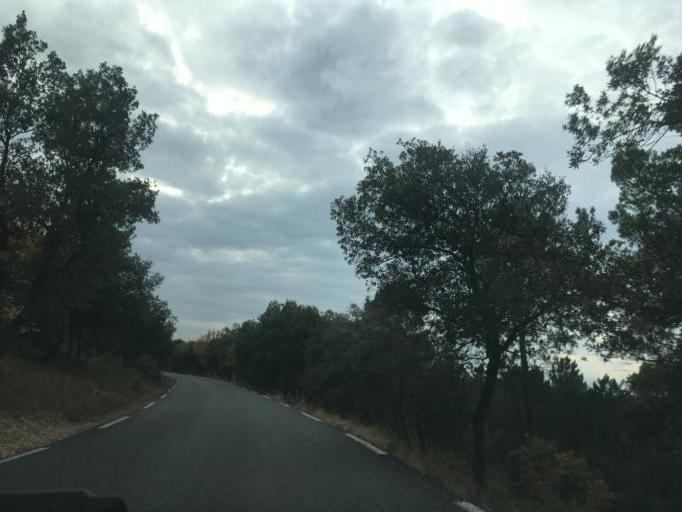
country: FR
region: Provence-Alpes-Cote d'Azur
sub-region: Departement du Var
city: Villecroze
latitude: 43.5601
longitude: 6.3311
